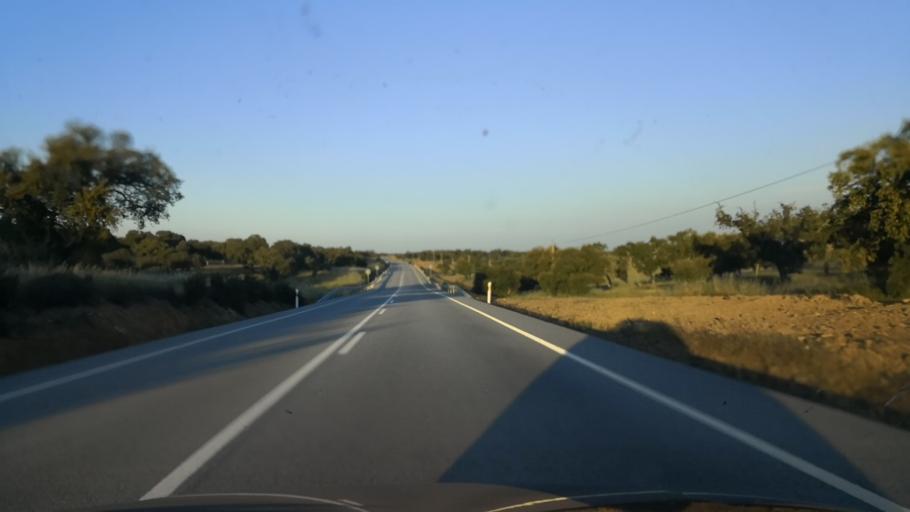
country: ES
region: Extremadura
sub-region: Provincia de Caceres
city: Carbajo
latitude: 39.5071
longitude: -7.1319
